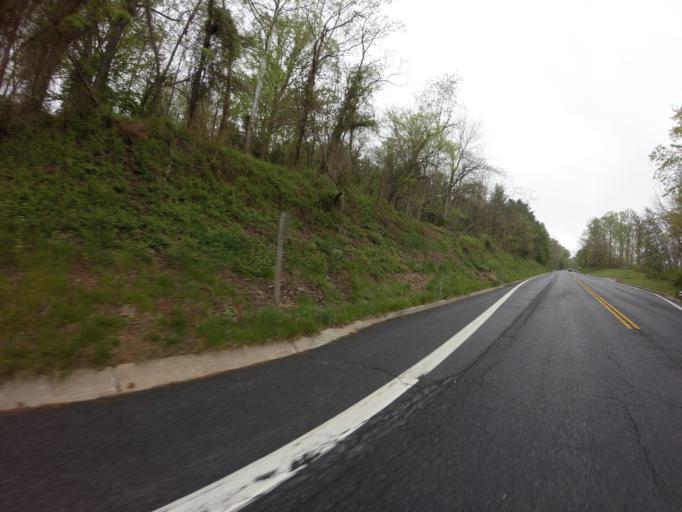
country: US
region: Maryland
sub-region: Frederick County
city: Myersville
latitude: 39.5028
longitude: -77.5488
